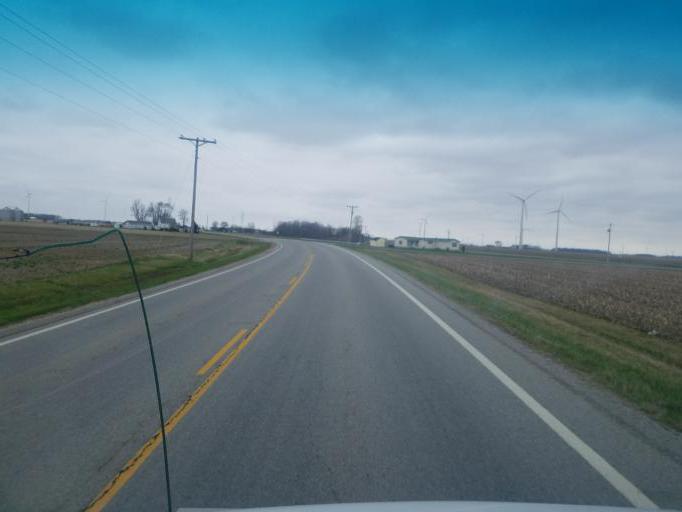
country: US
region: Ohio
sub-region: Van Wert County
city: Van Wert
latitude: 40.9315
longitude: -84.5126
